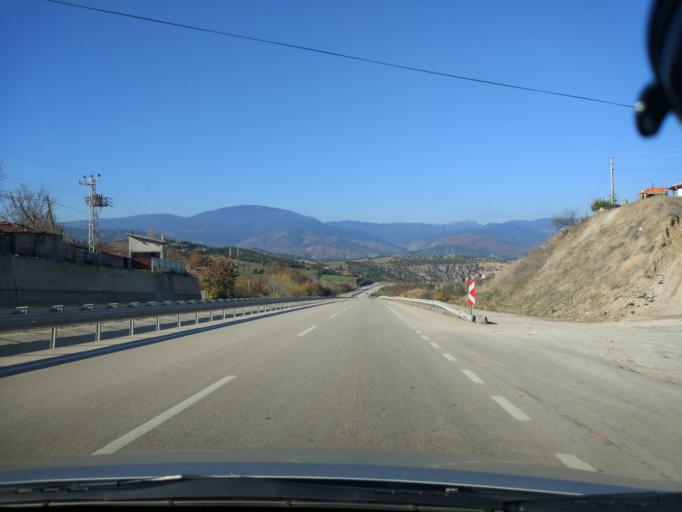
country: TR
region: Karabuk
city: Eskipazar
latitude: 40.9437
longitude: 32.5584
